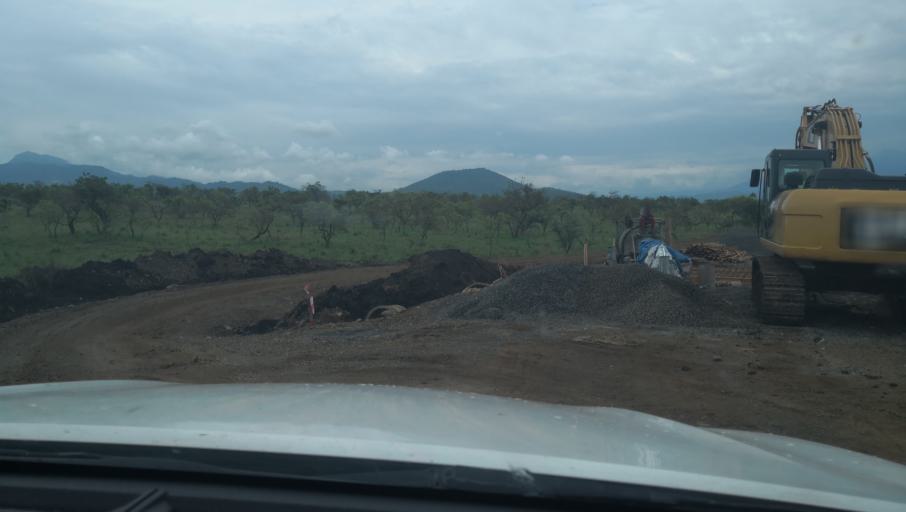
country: ET
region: Southern Nations, Nationalities, and People's Region
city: Felege Neway
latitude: 6.4233
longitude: 37.2396
